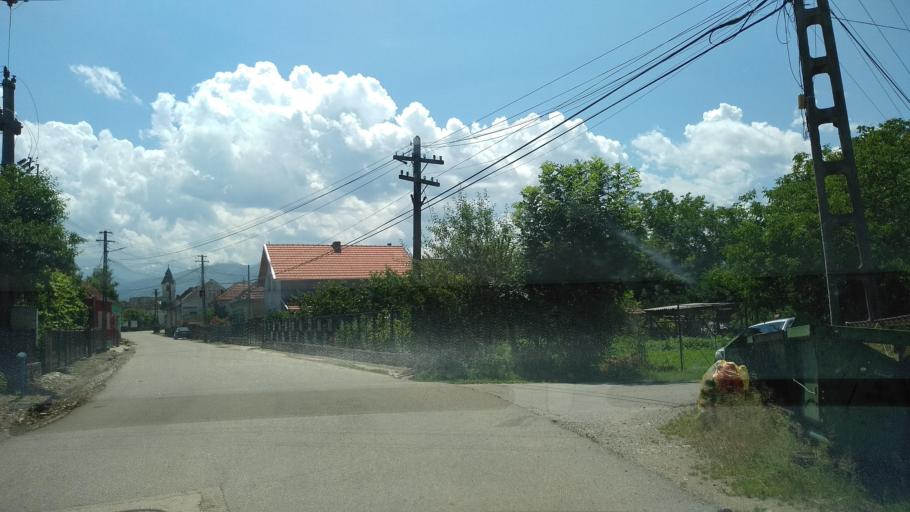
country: RO
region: Hunedoara
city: Densus
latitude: 45.5504
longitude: 22.8228
